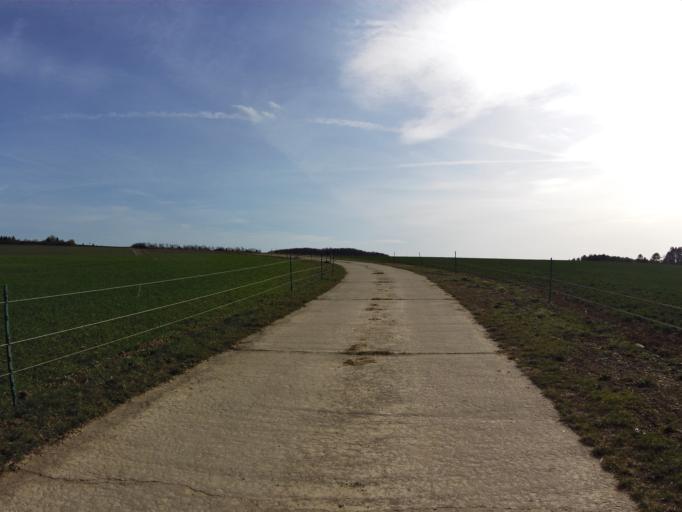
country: DE
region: Bavaria
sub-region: Regierungsbezirk Unterfranken
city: Greussenheim
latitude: 49.8360
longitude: 9.7964
